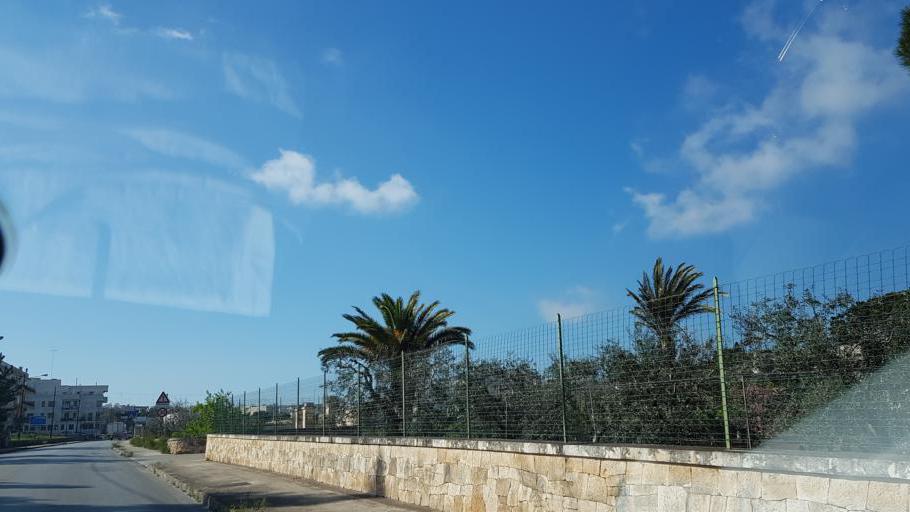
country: IT
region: Apulia
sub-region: Provincia di Brindisi
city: Ostuni
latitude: 40.7241
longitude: 17.5898
